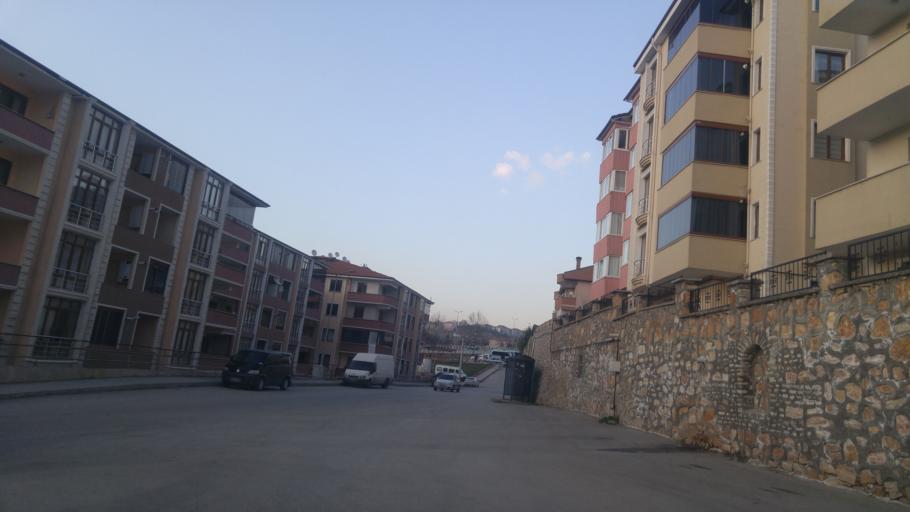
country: TR
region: Karabuk
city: Safranbolu
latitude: 41.2240
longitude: 32.6638
